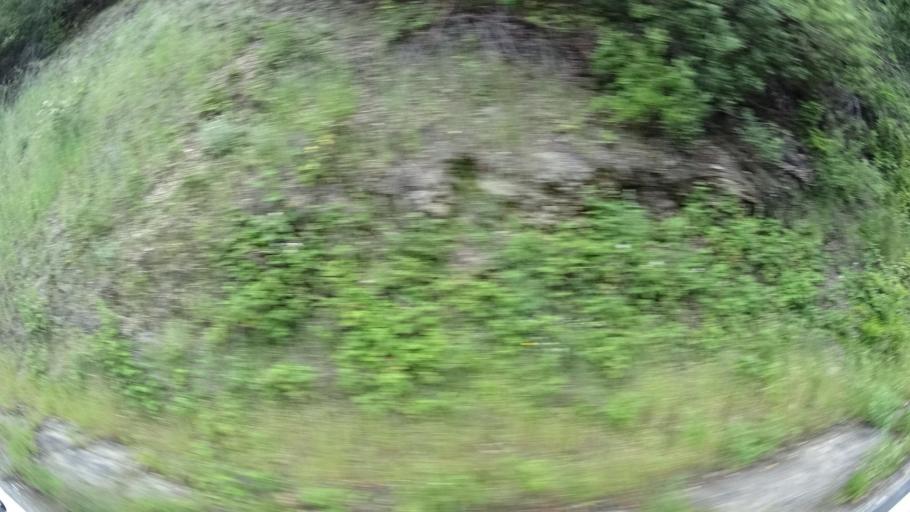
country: US
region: California
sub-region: Humboldt County
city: Willow Creek
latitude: 41.2562
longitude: -123.6278
